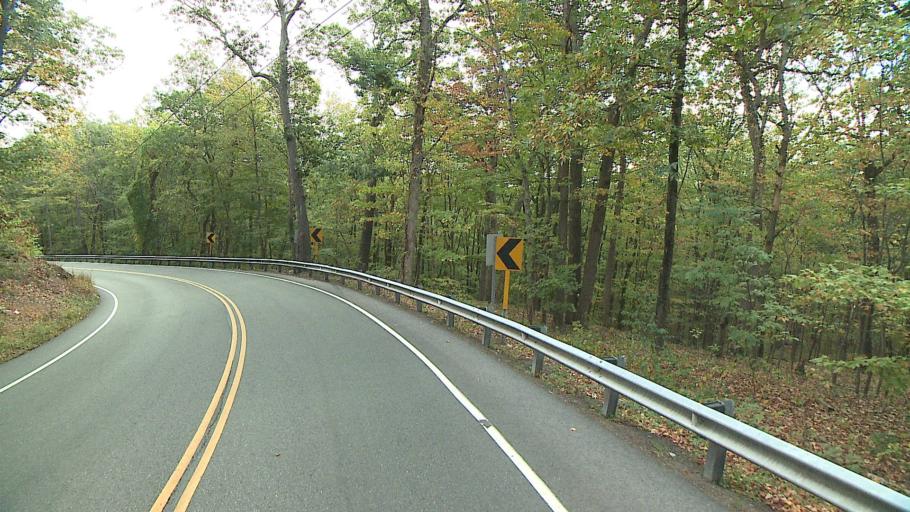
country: US
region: Connecticut
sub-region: New Haven County
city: Ansonia
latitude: 41.3546
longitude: -73.1037
